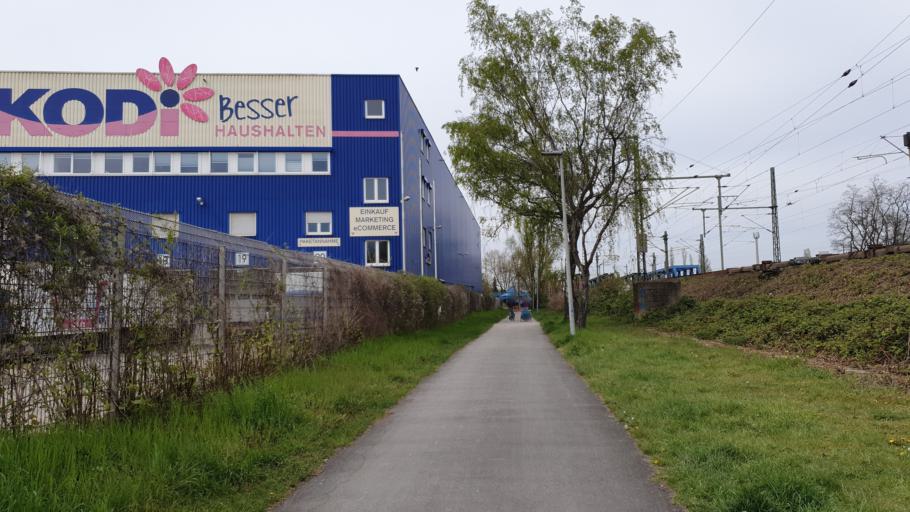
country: DE
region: North Rhine-Westphalia
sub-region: Regierungsbezirk Dusseldorf
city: Oberhausen
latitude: 51.4894
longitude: 6.8510
